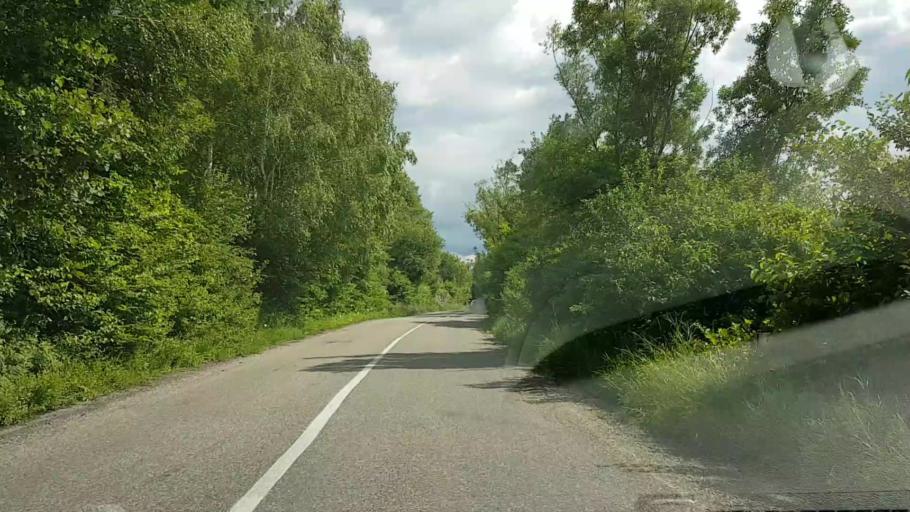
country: RO
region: Neamt
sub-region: Comuna Ceahlau
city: Ceahlau
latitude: 47.0683
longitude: 25.9607
